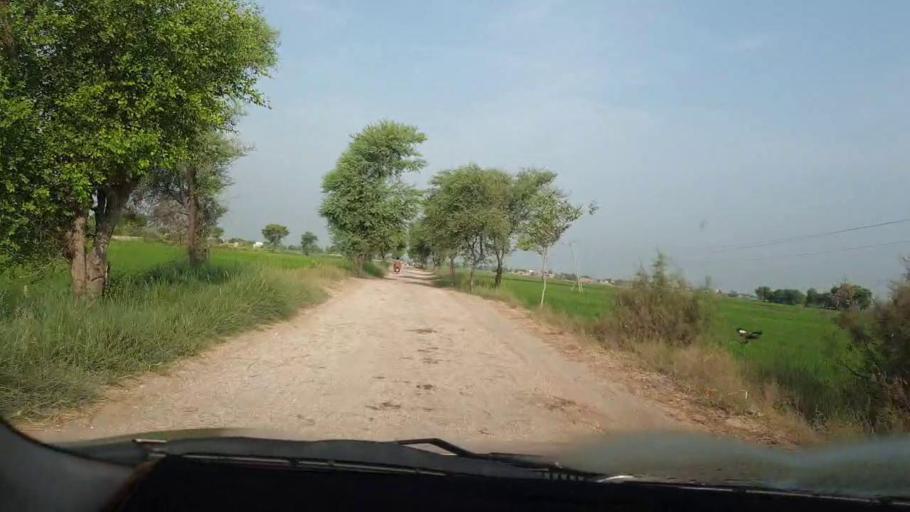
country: PK
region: Sindh
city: Goth Garelo
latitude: 27.4829
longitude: 68.0759
